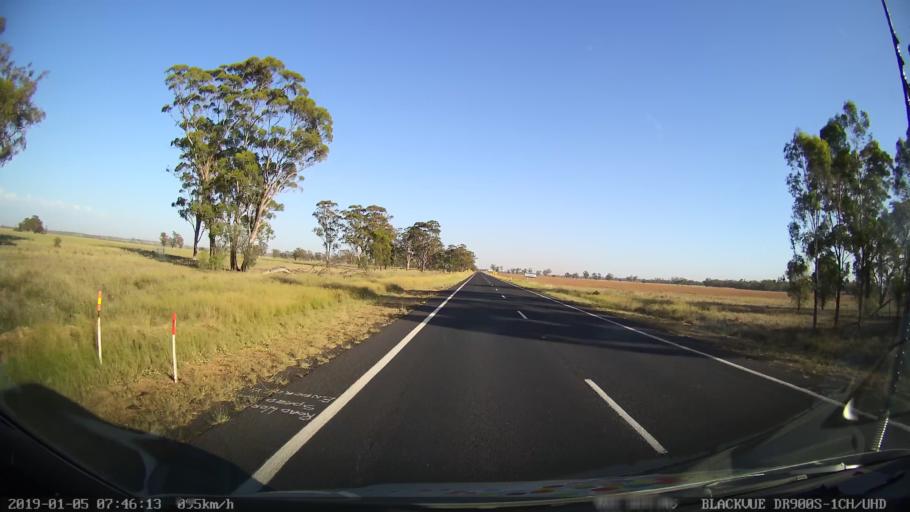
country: AU
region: New South Wales
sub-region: Gilgandra
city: Gilgandra
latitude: -31.8474
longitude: 148.6443
